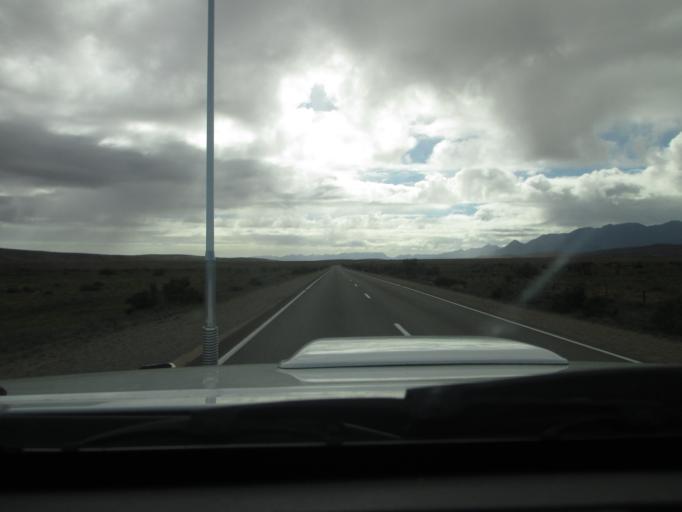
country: AU
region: South Australia
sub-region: Flinders Ranges
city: Quorn
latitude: -31.6085
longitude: 138.3990
